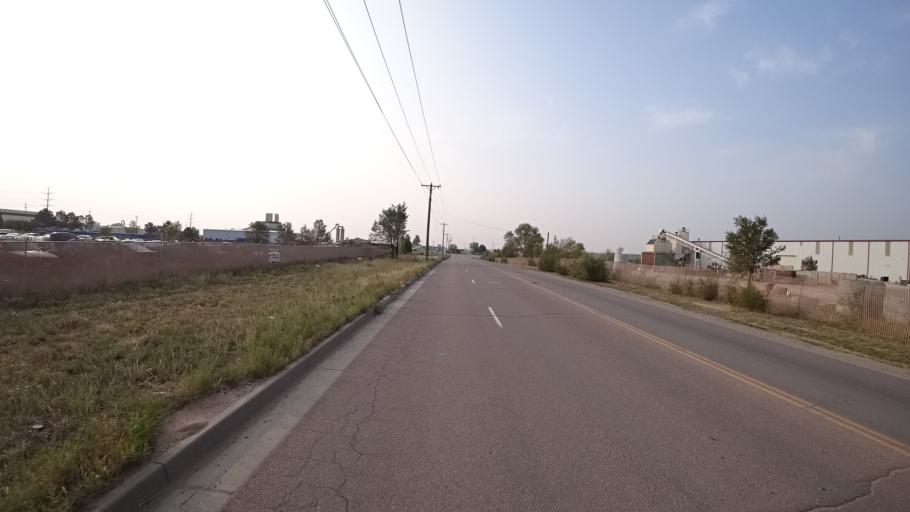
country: US
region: Colorado
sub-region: El Paso County
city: Stratmoor
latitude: 38.7808
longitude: -104.7733
